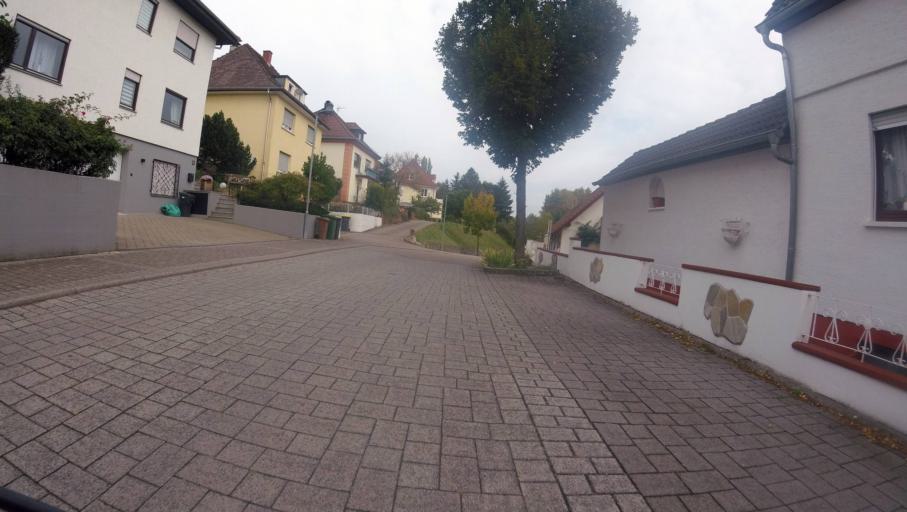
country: DE
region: Baden-Wuerttemberg
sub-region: Karlsruhe Region
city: Gernsbach
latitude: 48.7680
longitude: 8.3334
